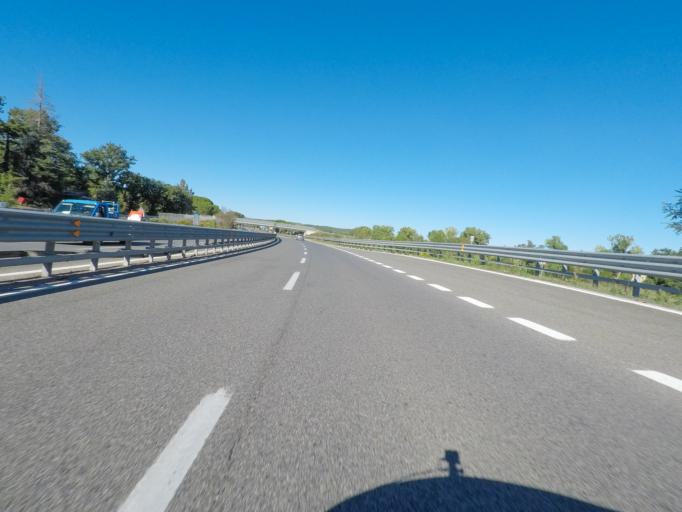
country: IT
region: Tuscany
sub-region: Provincia di Grosseto
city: Campagnatico
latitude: 42.9244
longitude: 11.2639
